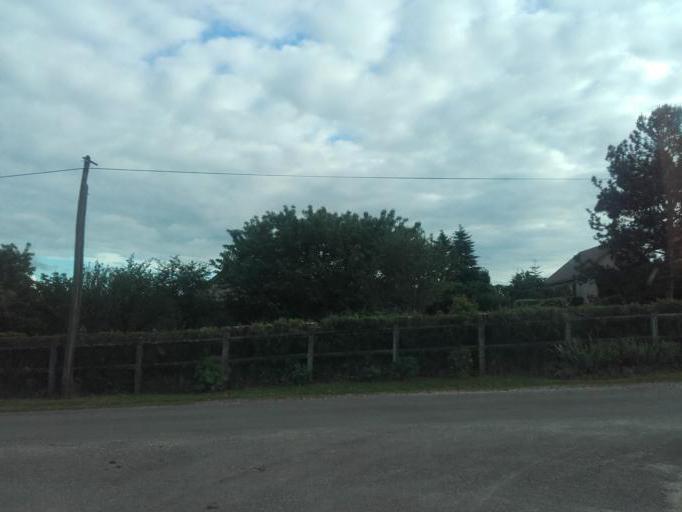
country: FR
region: Bourgogne
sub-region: Departement de Saone-et-Loire
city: Rully
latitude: 46.8684
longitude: 4.7441
